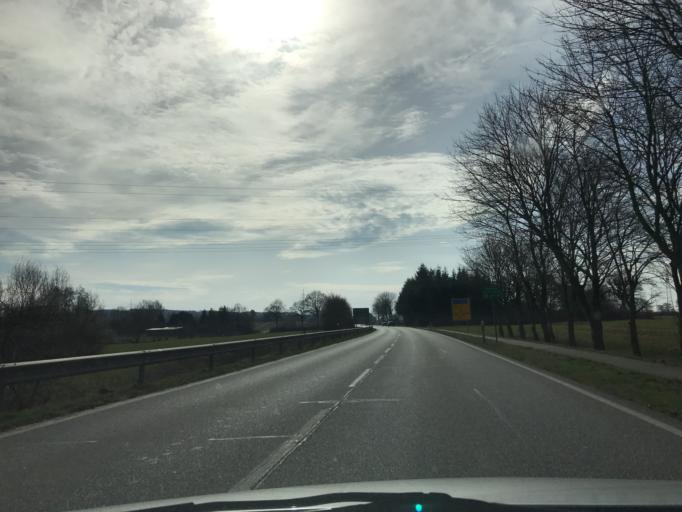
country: DE
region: Schleswig-Holstein
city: Goosefeld
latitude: 54.4307
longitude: 9.8097
